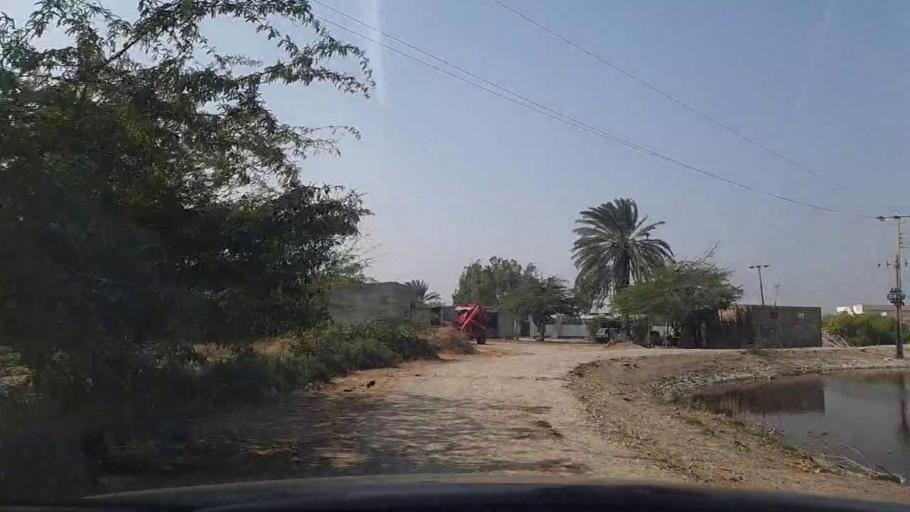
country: PK
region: Sindh
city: Mirpur Sakro
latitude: 24.5625
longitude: 67.7758
